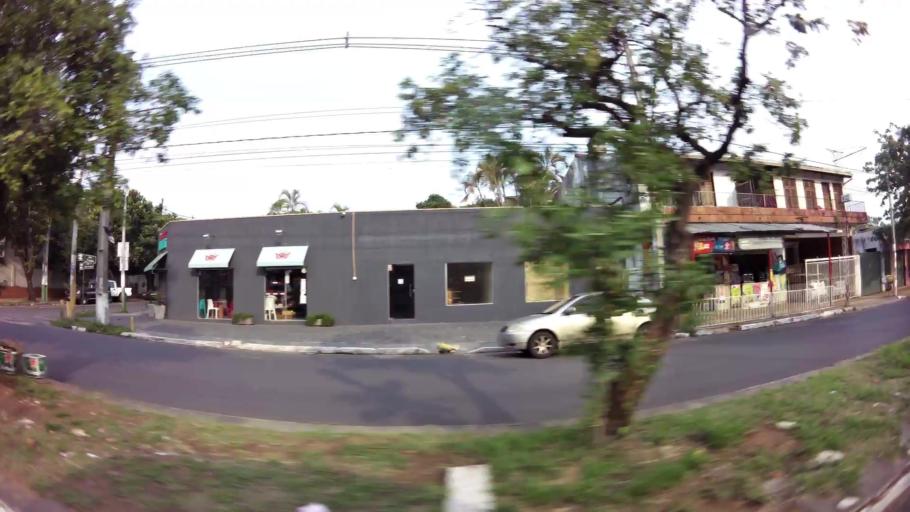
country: PY
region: Asuncion
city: Asuncion
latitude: -25.3079
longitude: -57.6090
